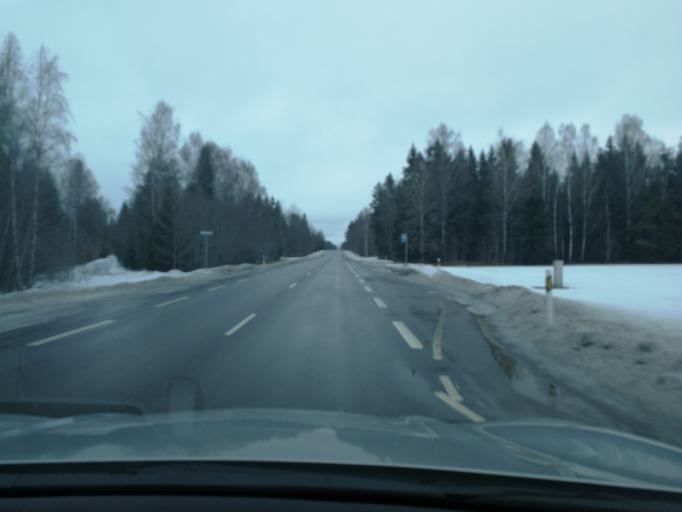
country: EE
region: Harju
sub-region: Anija vald
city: Kehra
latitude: 59.2336
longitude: 25.2846
